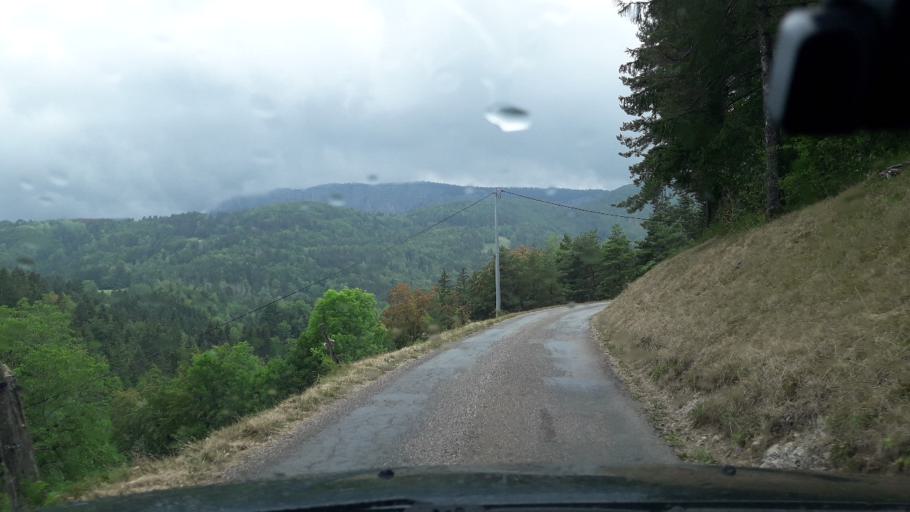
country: FR
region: Rhone-Alpes
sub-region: Departement de la Savoie
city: Vimines
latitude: 45.4641
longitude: 5.8898
